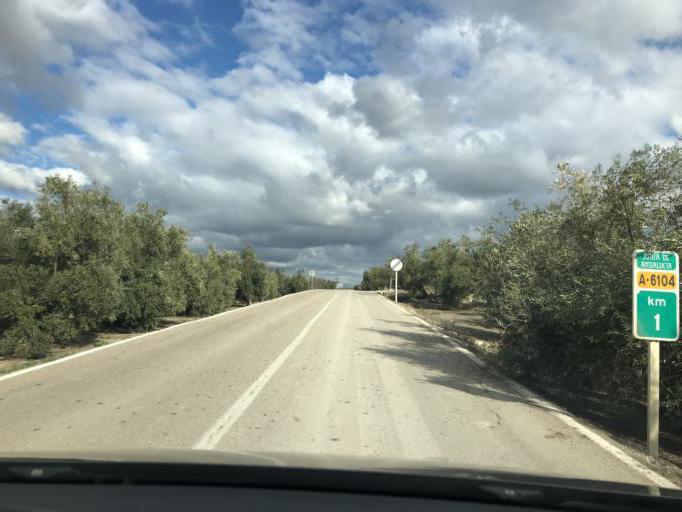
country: ES
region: Andalusia
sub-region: Provincia de Jaen
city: Ubeda
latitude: 37.9890
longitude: -3.3939
